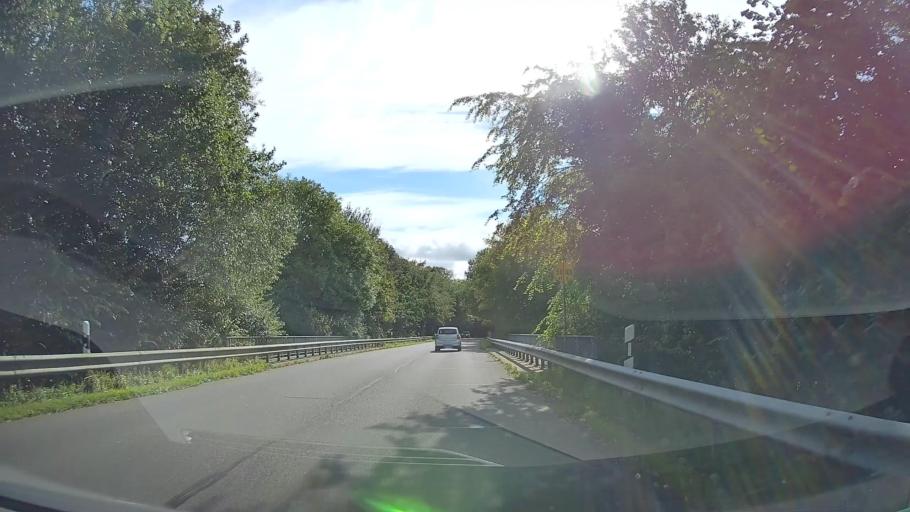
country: DE
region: Schleswig-Holstein
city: Glucksburg
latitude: 54.8471
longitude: 9.5862
